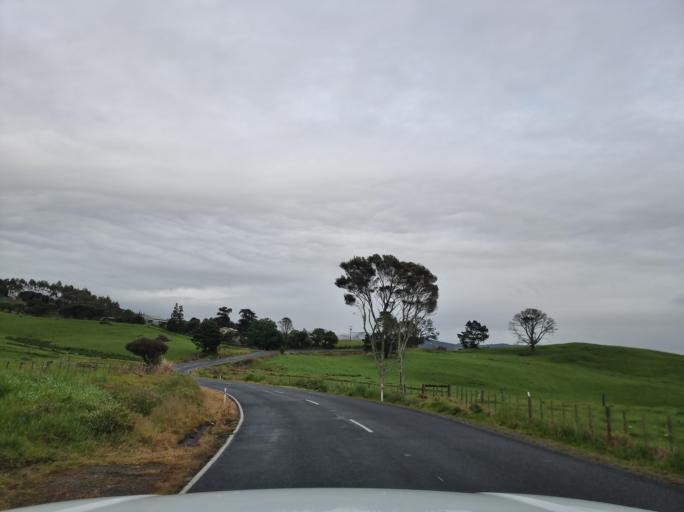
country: NZ
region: Northland
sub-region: Whangarei
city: Ruakaka
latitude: -35.9689
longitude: 174.4247
